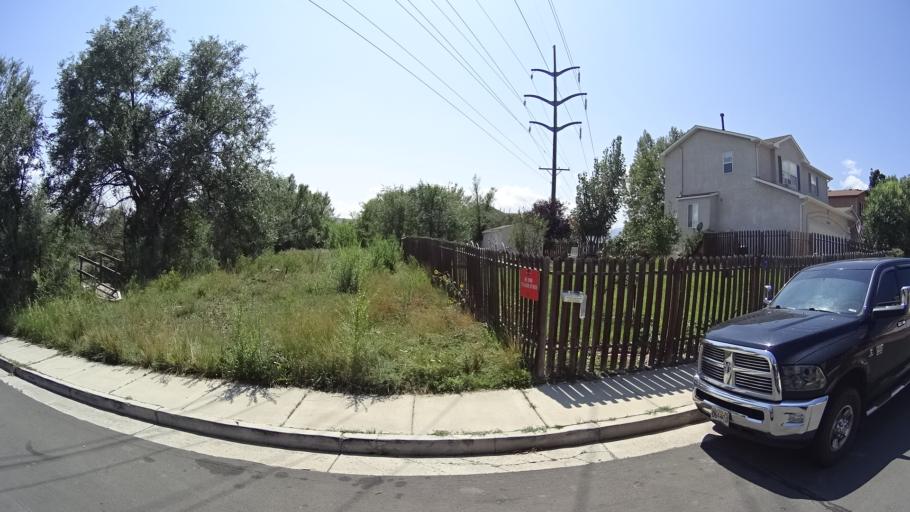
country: US
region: Colorado
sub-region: El Paso County
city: Colorado Springs
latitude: 38.8696
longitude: -104.8390
